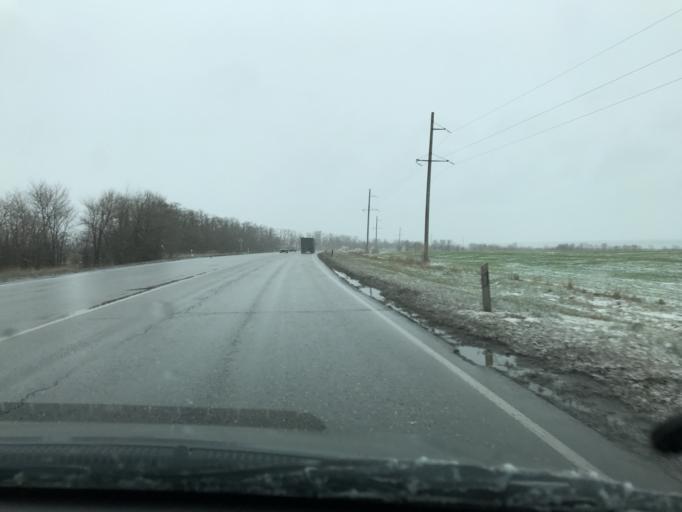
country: RU
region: Rostov
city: Mechetinskaya
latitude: 46.7882
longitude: 40.4048
